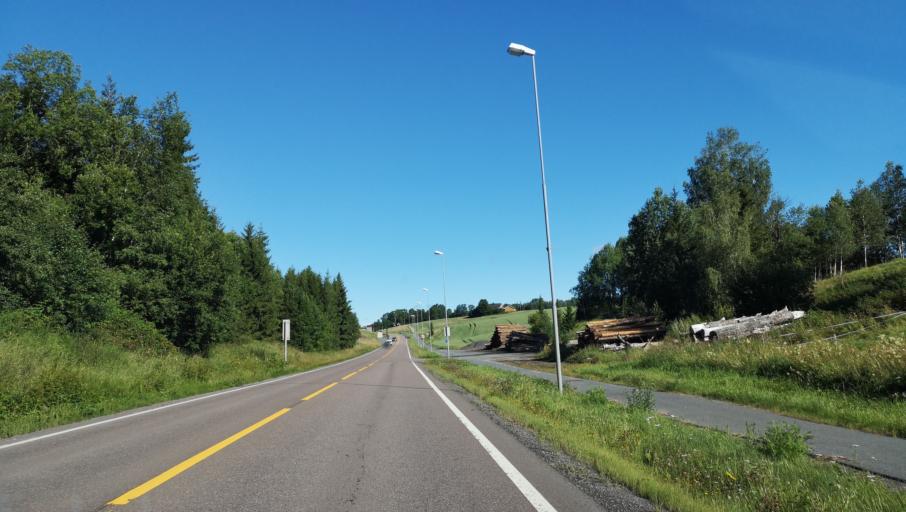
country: NO
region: Ostfold
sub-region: Spydeberg
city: Spydeberg
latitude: 59.6065
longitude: 11.0990
